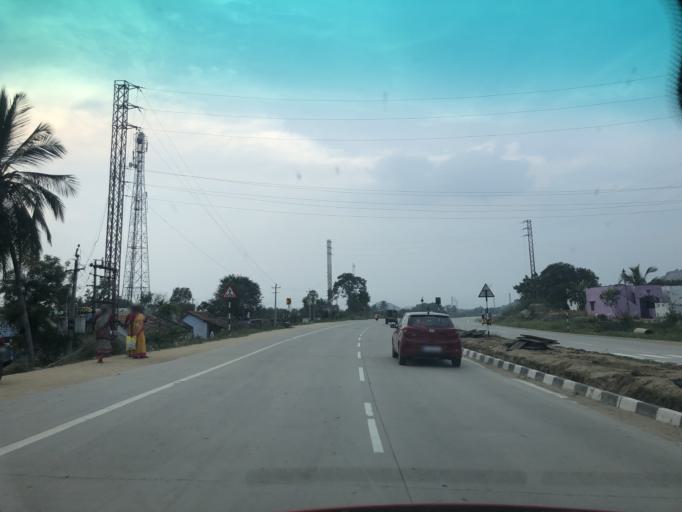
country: IN
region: Andhra Pradesh
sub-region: Chittoor
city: Chittoor
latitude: 13.1958
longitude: 79.0043
